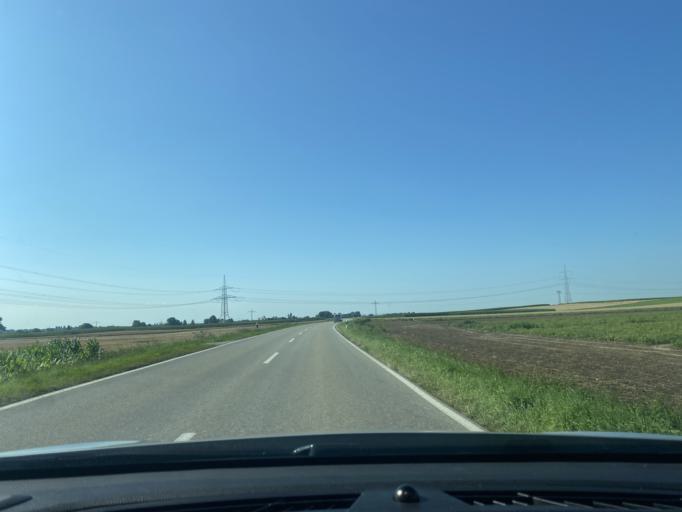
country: DE
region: Bavaria
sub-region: Upper Bavaria
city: Eitting
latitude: 48.3468
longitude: 11.8974
